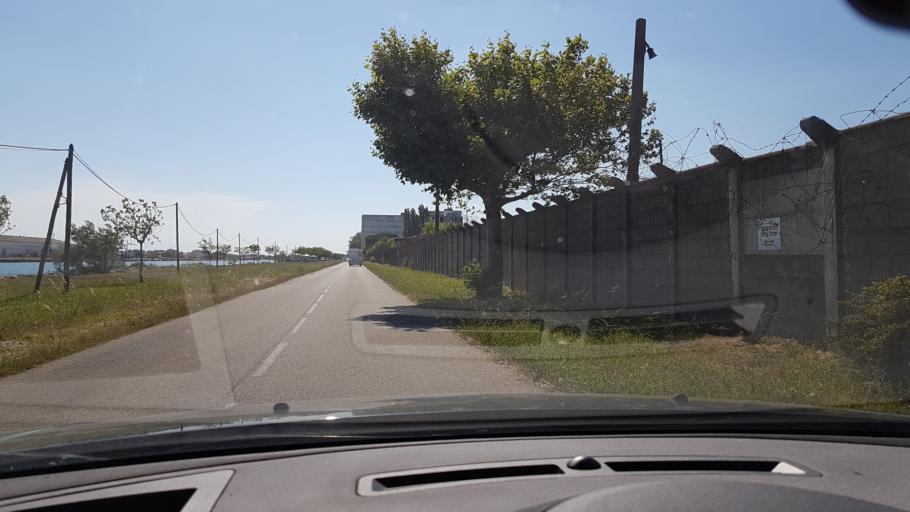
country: FR
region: Provence-Alpes-Cote d'Azur
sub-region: Departement des Bouches-du-Rhone
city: Port-Saint-Louis-du-Rhone
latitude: 43.3873
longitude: 4.8266
